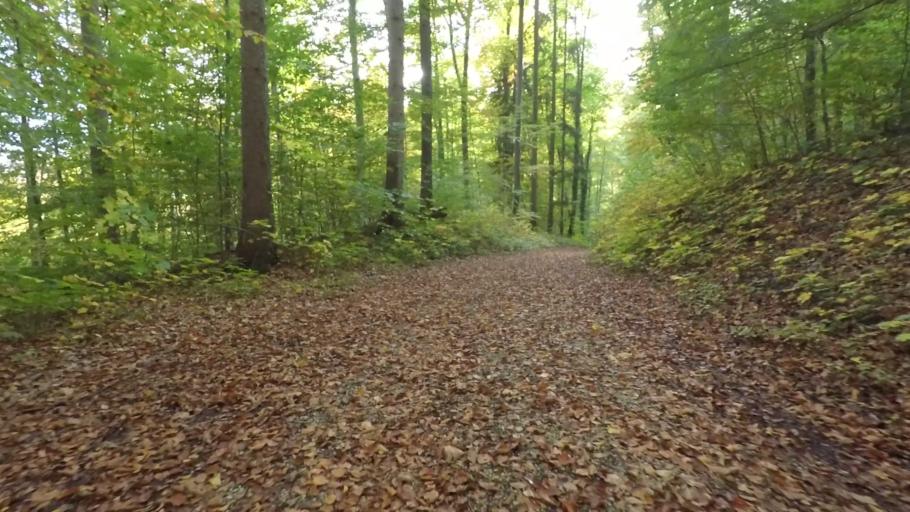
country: DE
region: Baden-Wuerttemberg
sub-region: Tuebingen Region
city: Pfullingen
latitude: 48.4429
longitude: 9.2335
